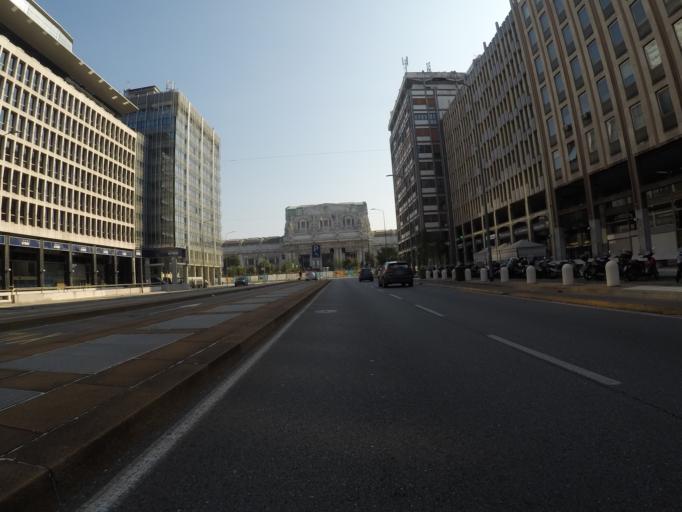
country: IT
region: Lombardy
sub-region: Citta metropolitana di Milano
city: Milano
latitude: 45.4831
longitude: 9.2017
